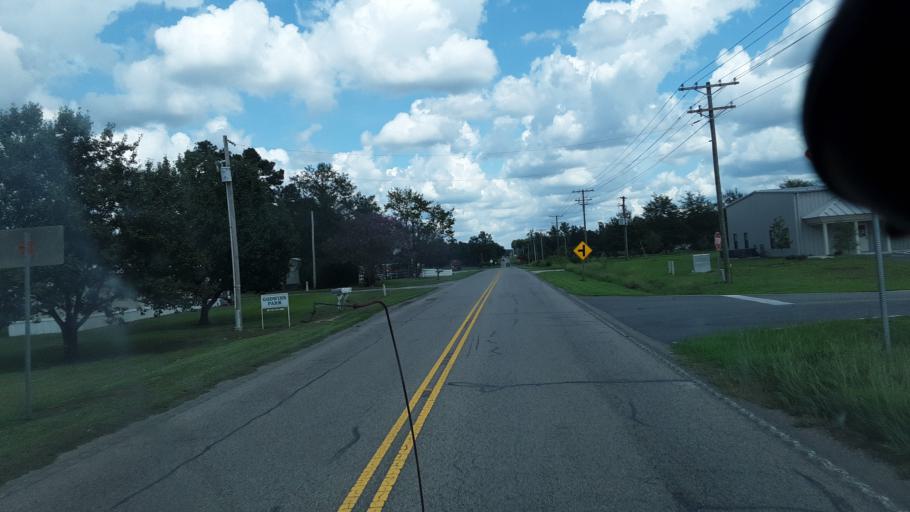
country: US
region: South Carolina
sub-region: Williamsburg County
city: Andrews
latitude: 33.5039
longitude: -79.5234
